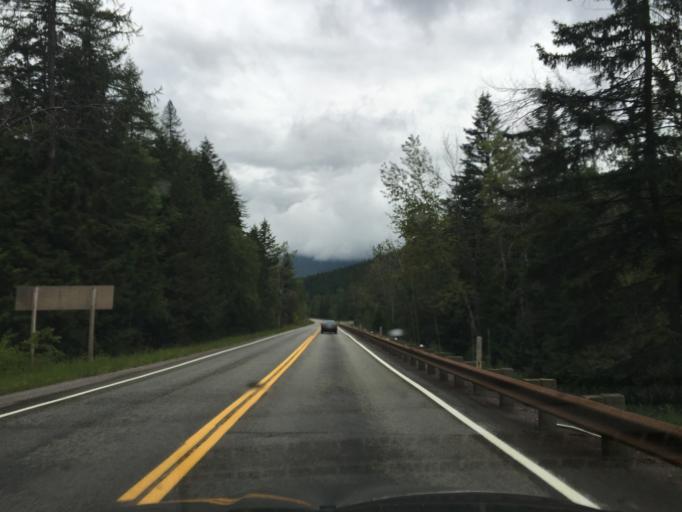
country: US
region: Montana
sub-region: Flathead County
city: Columbia Falls
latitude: 48.4968
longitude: -113.9630
